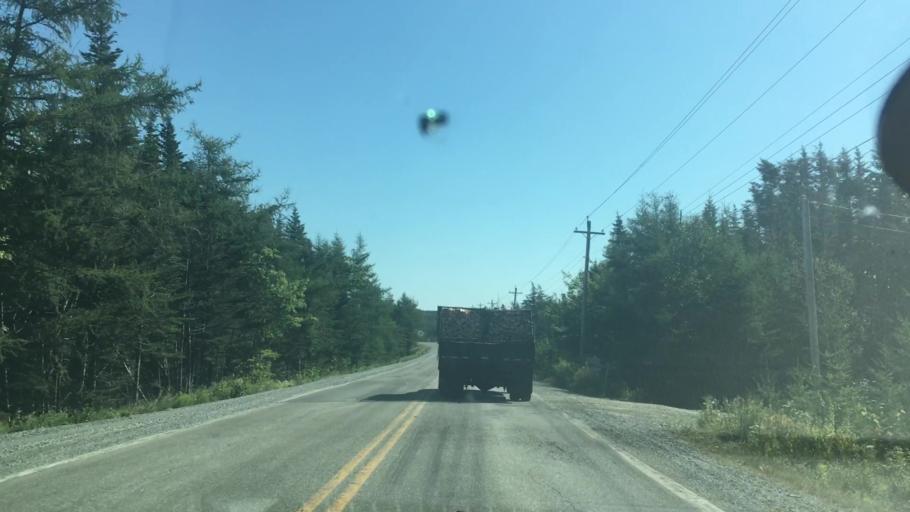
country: CA
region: Nova Scotia
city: New Glasgow
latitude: 44.9037
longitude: -62.4604
